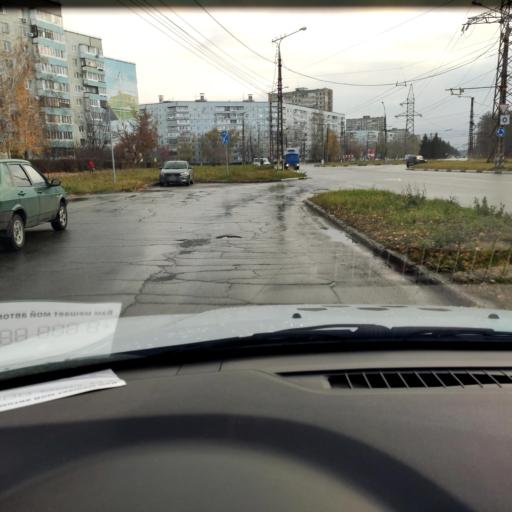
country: RU
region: Samara
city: Tol'yatti
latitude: 53.5041
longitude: 49.4301
